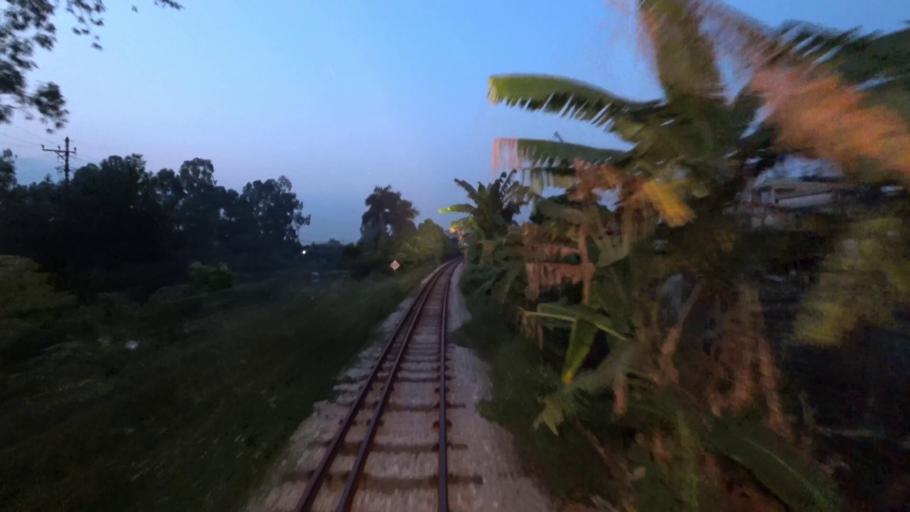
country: VN
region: Ha Noi
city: Soc Son
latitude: 21.2497
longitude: 105.8617
